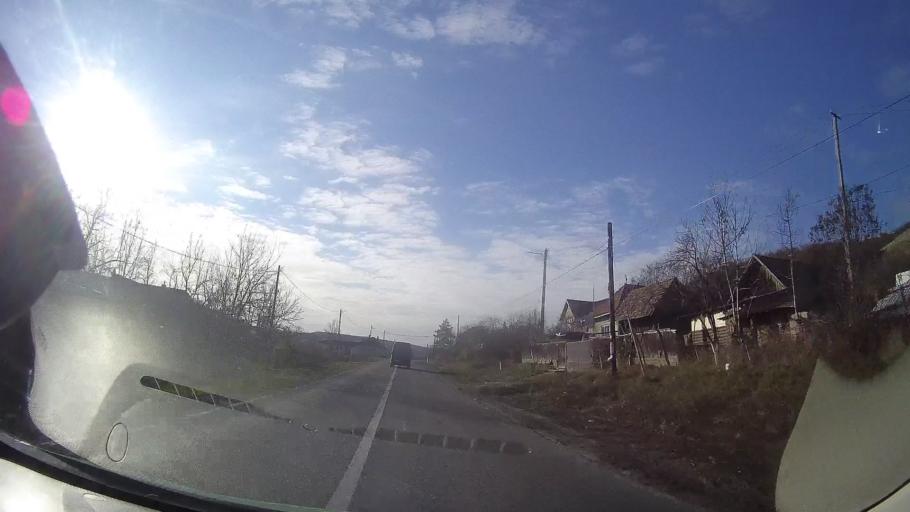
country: RO
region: Cluj
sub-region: Comuna Caianu
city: Caianu
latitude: 46.7981
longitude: 23.9198
